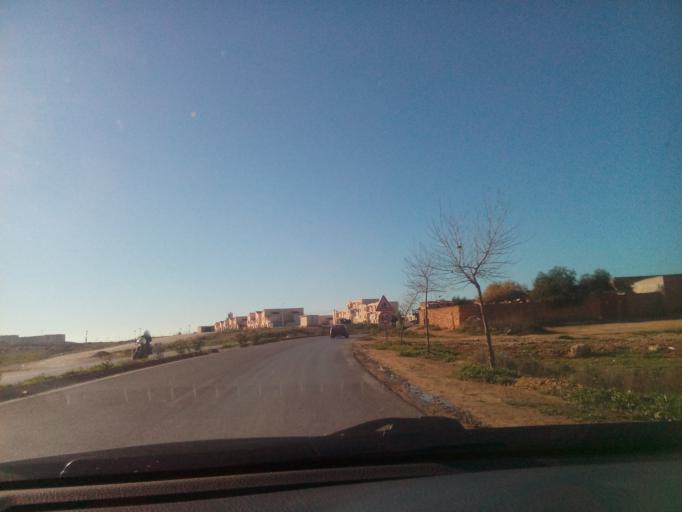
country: DZ
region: Relizane
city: Relizane
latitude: 35.7090
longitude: 0.5117
